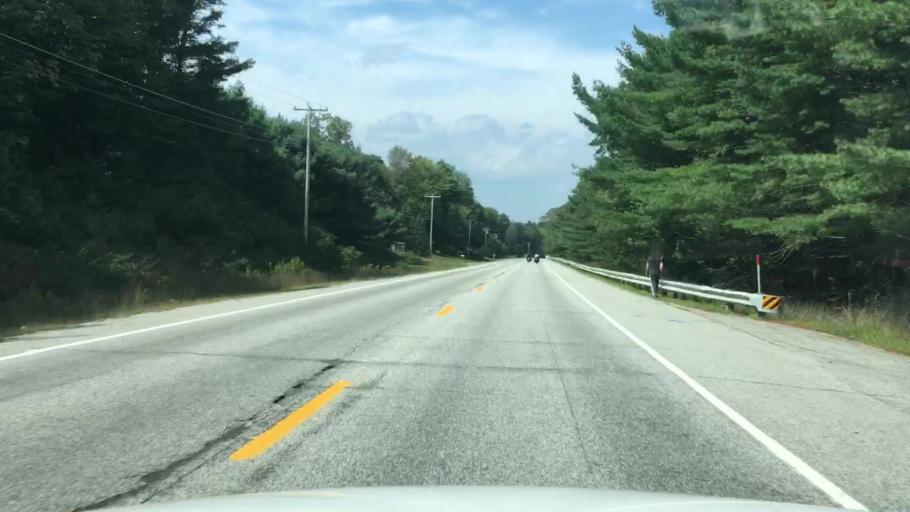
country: US
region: Maine
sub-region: Oxford County
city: Peru
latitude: 44.4980
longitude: -70.3943
